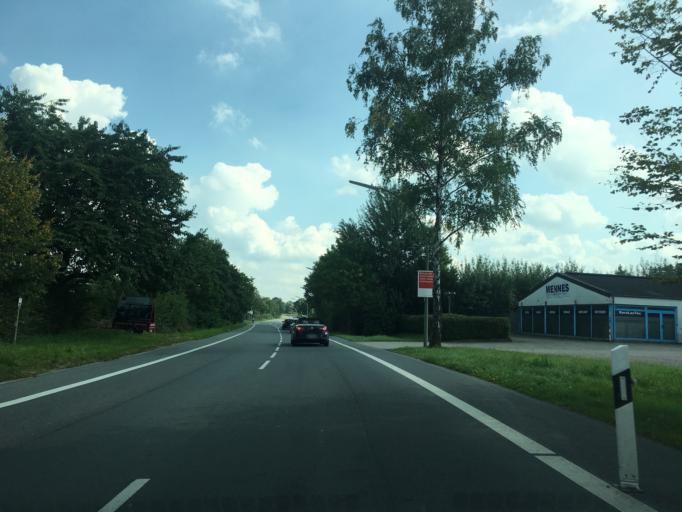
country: DE
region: North Rhine-Westphalia
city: Selm
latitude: 51.6949
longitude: 7.4805
